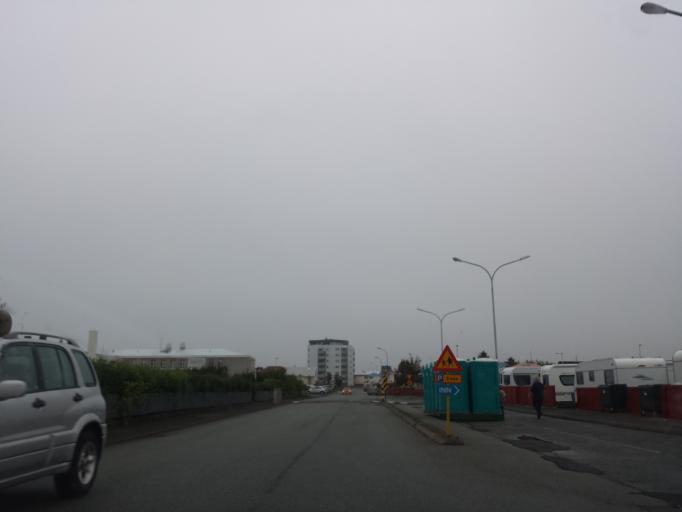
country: IS
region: Southern Peninsula
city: Reykjanesbaer
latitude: 64.0018
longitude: -22.5574
